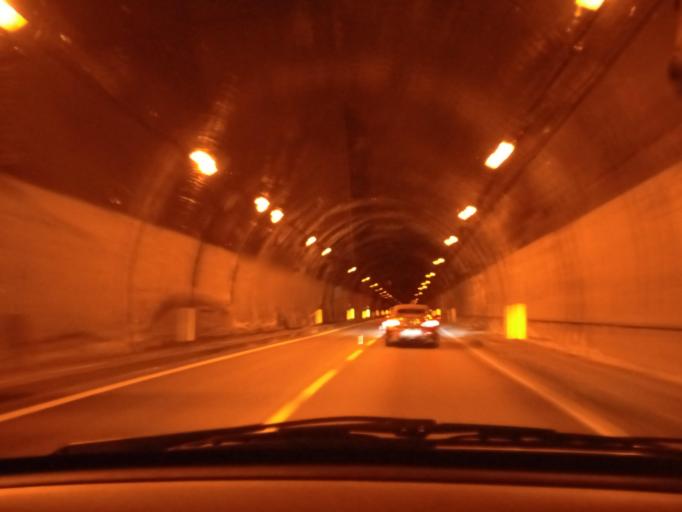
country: IT
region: Sicily
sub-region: Messina
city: Gioiosa Marea
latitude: 38.1565
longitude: 14.9020
